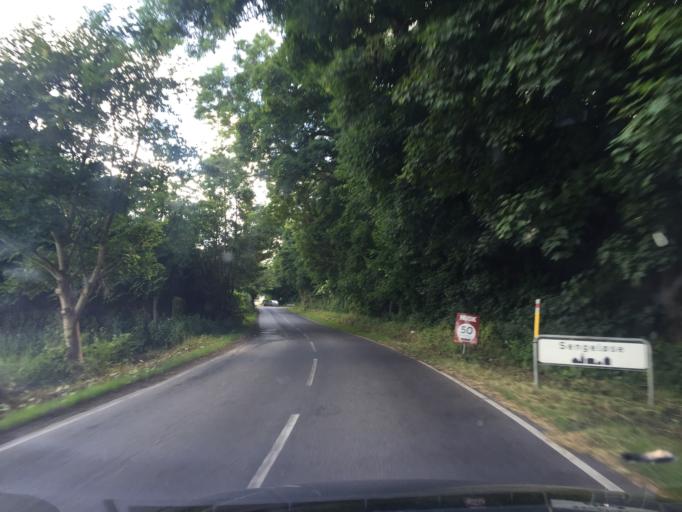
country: DK
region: Capital Region
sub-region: Hoje-Taastrup Kommune
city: Taastrup
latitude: 55.6935
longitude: 12.2475
